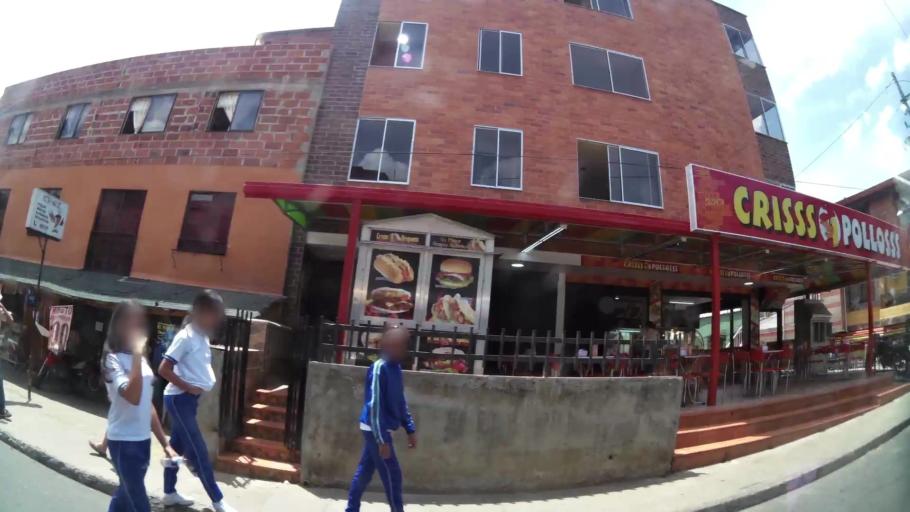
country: CO
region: Antioquia
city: Bello
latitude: 6.3460
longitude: -75.5473
